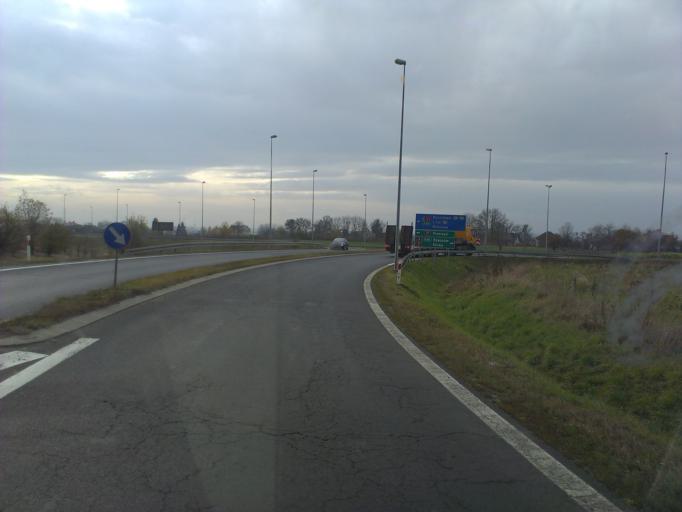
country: PL
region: Subcarpathian Voivodeship
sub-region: Powiat jaroslawski
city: Radymno
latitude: 49.9314
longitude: 22.8221
